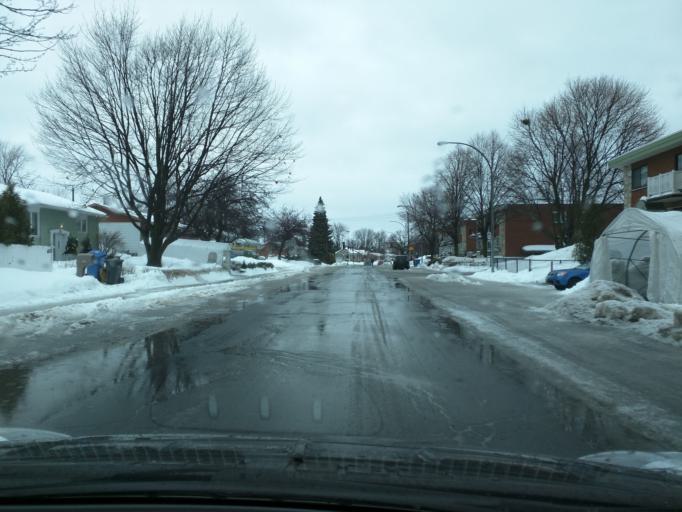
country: CA
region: Quebec
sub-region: Monteregie
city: Longueuil
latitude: 45.5289
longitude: -73.4585
